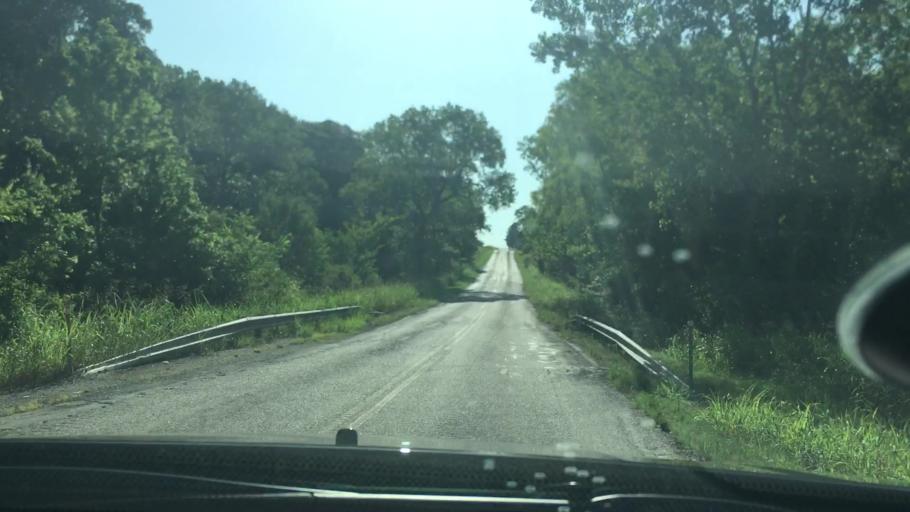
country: US
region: Oklahoma
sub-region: Pontotoc County
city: Ada
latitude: 34.8107
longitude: -96.6432
